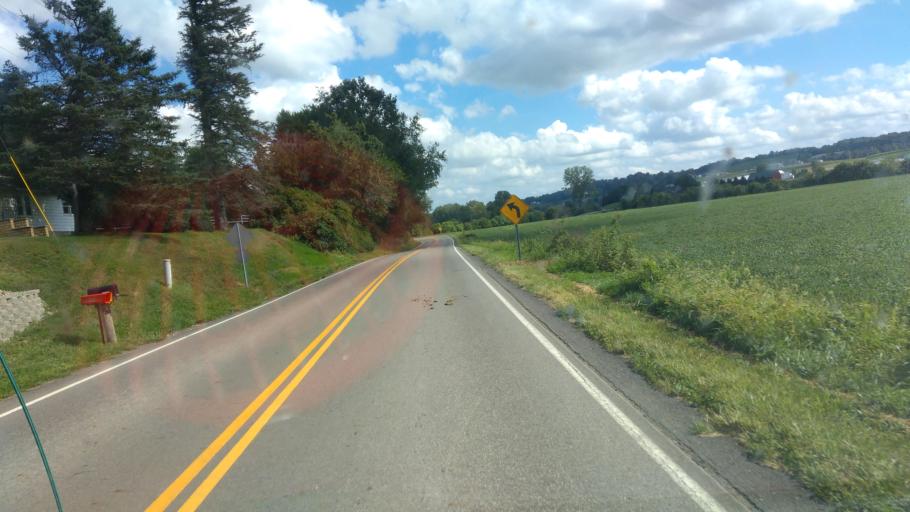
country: US
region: Ohio
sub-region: Holmes County
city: Millersburg
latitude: 40.6235
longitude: -81.8858
